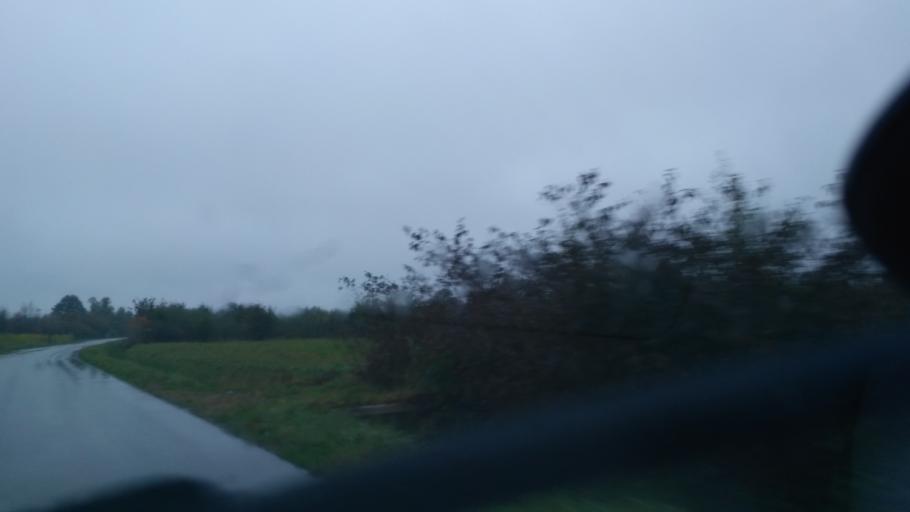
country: PL
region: Subcarpathian Voivodeship
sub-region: Powiat krosnienski
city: Kroscienko Wyzne
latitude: 49.6651
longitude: 21.8040
